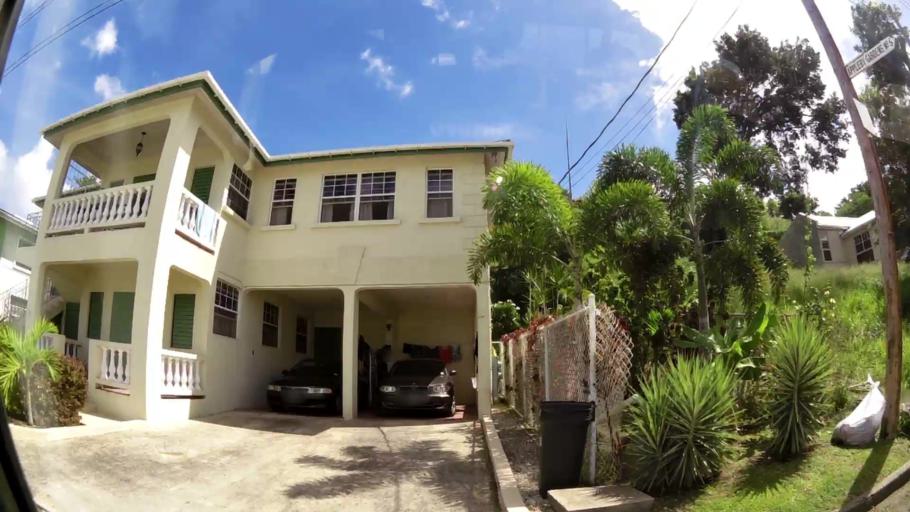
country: BB
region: Saint James
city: Holetown
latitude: 13.1550
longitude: -59.6337
